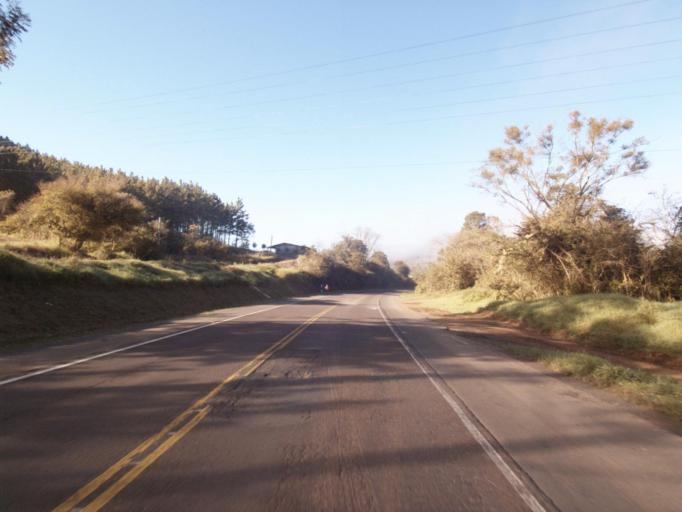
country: BR
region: Rio Grande do Sul
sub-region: Frederico Westphalen
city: Frederico Westphalen
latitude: -26.9740
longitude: -53.2144
